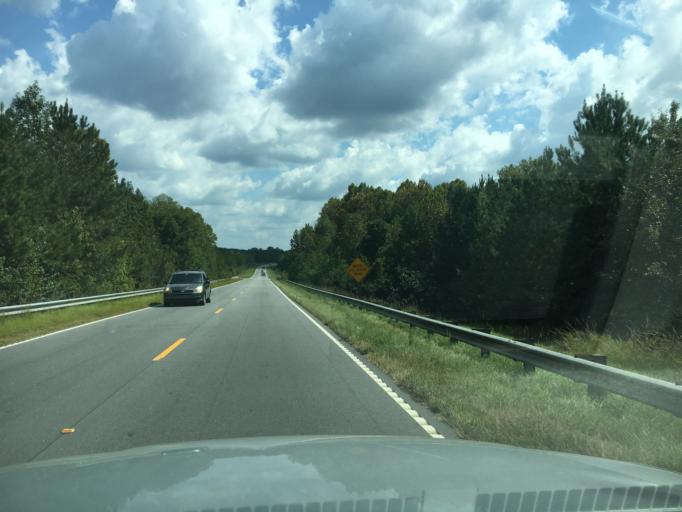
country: US
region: South Carolina
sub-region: Greenwood County
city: Greenwood
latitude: 34.1537
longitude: -82.1658
